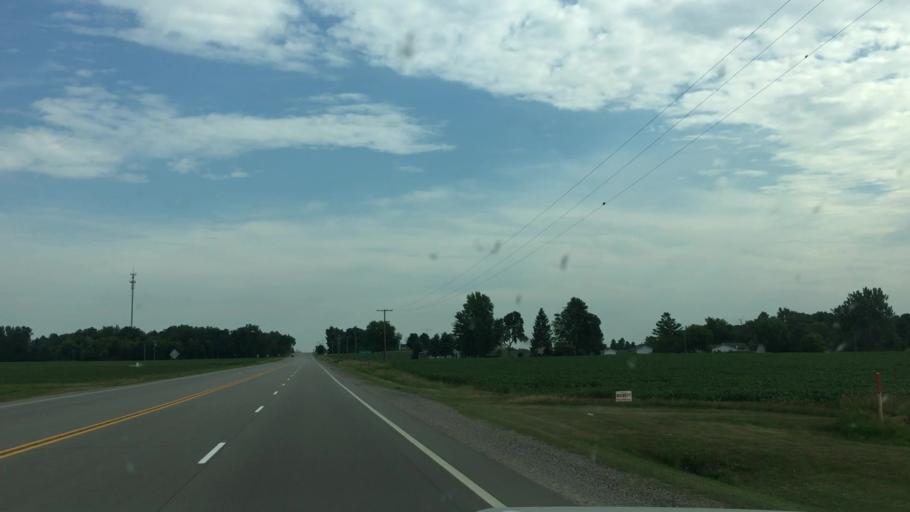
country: US
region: Michigan
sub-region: Sanilac County
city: Marlette
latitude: 43.3890
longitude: -83.0863
